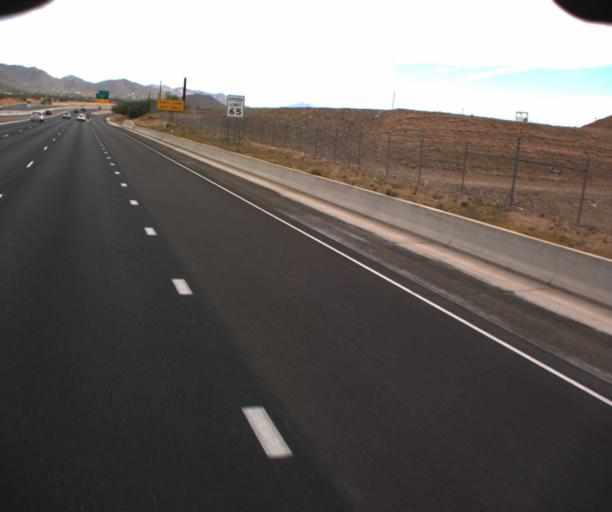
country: US
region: Arizona
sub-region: Maricopa County
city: Mesa
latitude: 33.4809
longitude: -111.7286
